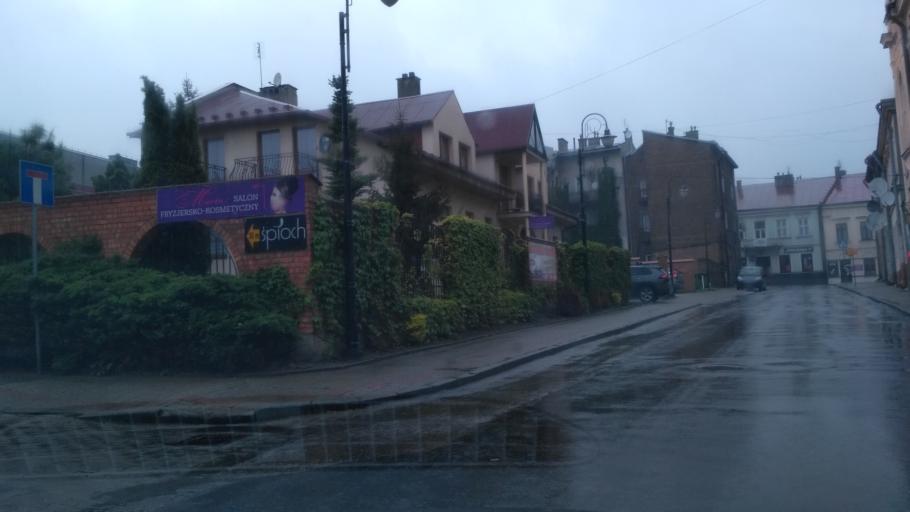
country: PL
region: Subcarpathian Voivodeship
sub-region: Powiat jaroslawski
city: Jaroslaw
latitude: 50.0181
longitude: 22.6867
